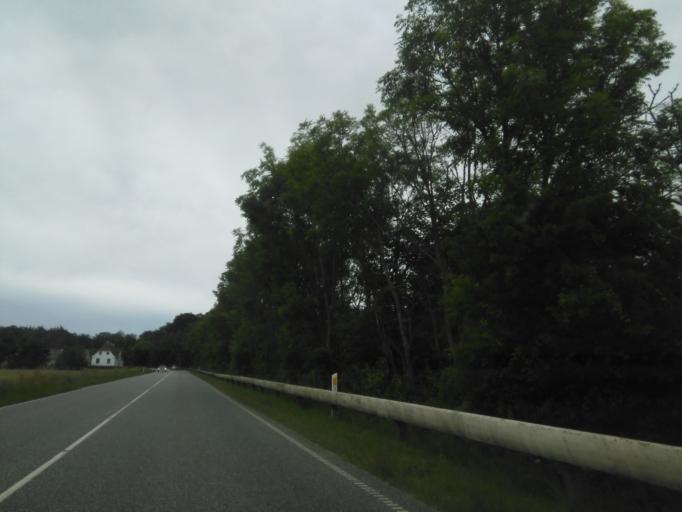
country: DK
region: Central Jutland
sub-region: Skanderborg Kommune
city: Skanderborg
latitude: 55.9559
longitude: 9.9806
